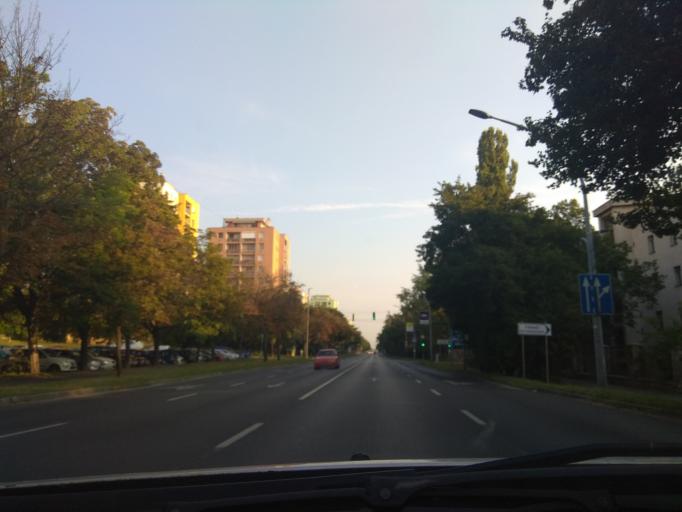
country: HU
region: Borsod-Abauj-Zemplen
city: Miskolc
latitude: 48.1169
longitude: 20.7897
